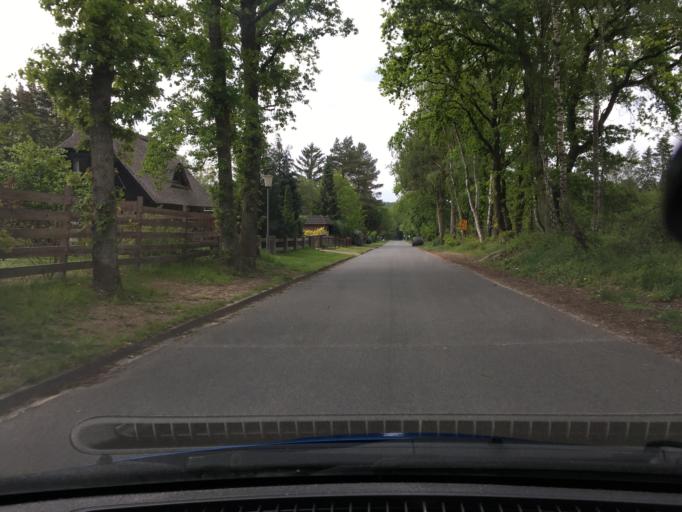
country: DE
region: Lower Saxony
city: Rehlingen
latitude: 53.1030
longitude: 10.2259
